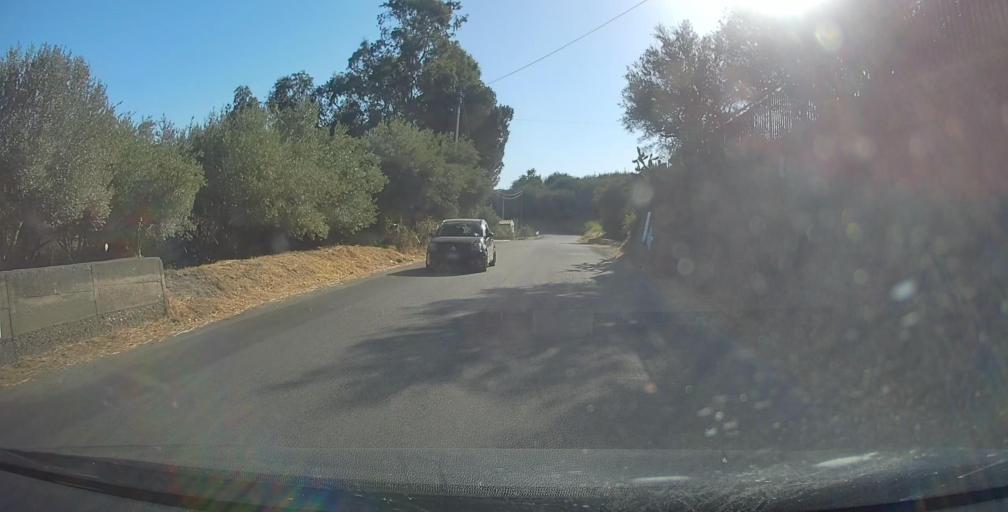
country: IT
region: Sicily
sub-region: Messina
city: Librizzi
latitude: 38.0769
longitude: 14.9730
